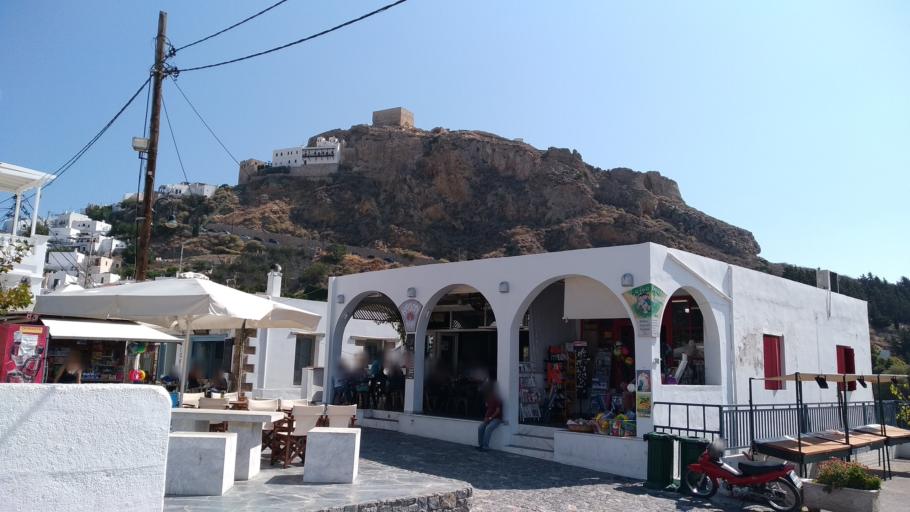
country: GR
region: Central Greece
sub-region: Nomos Evvoias
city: Skyros
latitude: 38.9045
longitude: 24.5648
